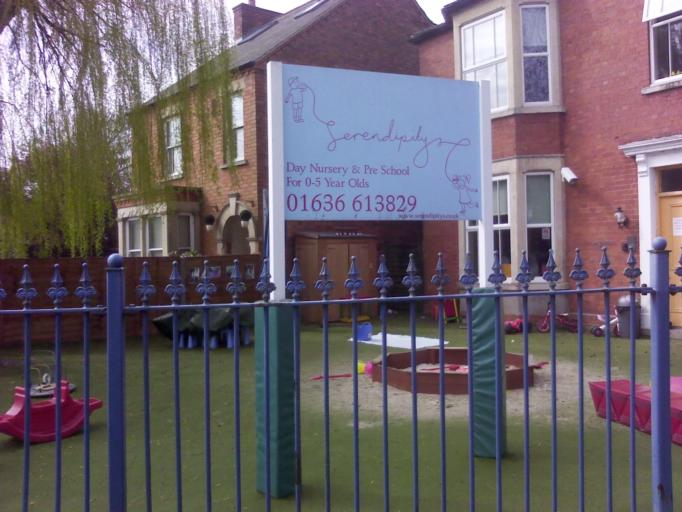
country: GB
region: England
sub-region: Nottinghamshire
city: Newark on Trent
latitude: 53.0813
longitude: -0.8011
